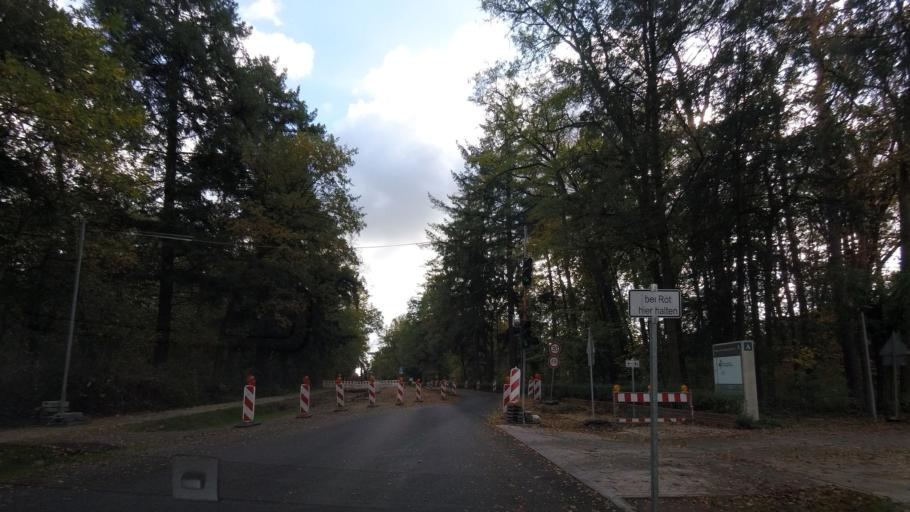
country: DE
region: Brandenburg
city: Beelitz
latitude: 52.2571
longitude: 12.9288
